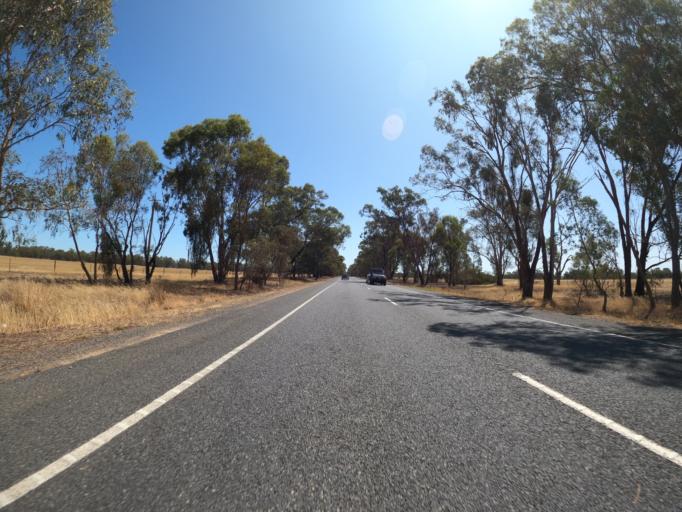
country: AU
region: New South Wales
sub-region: Corowa Shire
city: Corowa
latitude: -36.0619
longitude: 146.4055
